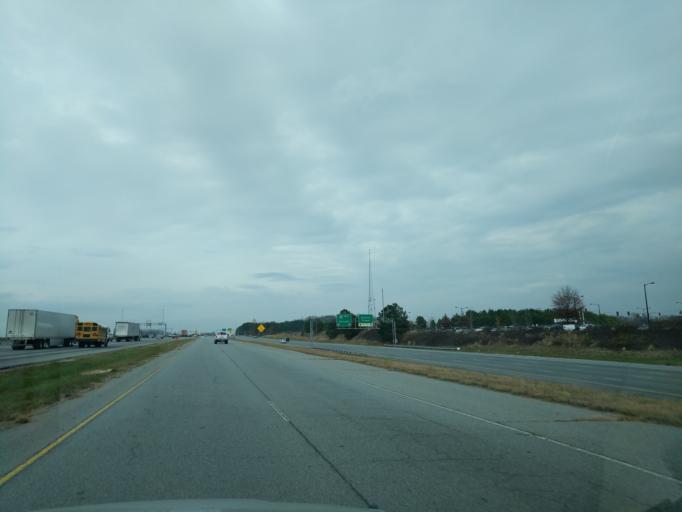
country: US
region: Georgia
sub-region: Gwinnett County
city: Duluth
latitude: 33.9805
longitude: -84.0871
